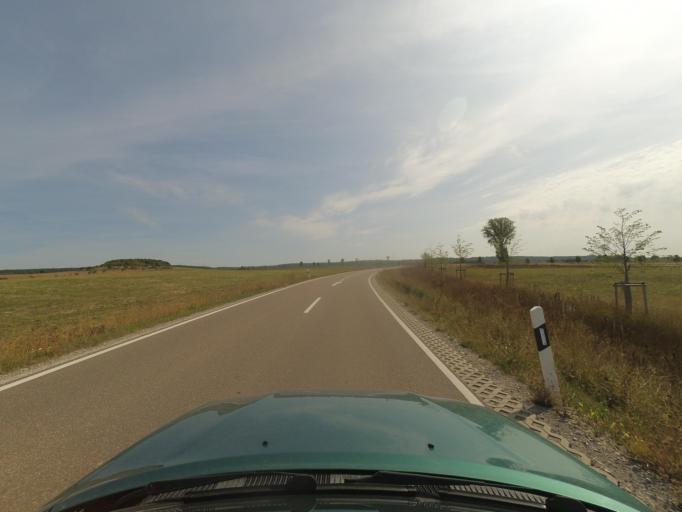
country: DE
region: Bavaria
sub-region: Regierungsbezirk Mittelfranken
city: Herrieden
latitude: 49.2321
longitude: 10.5186
